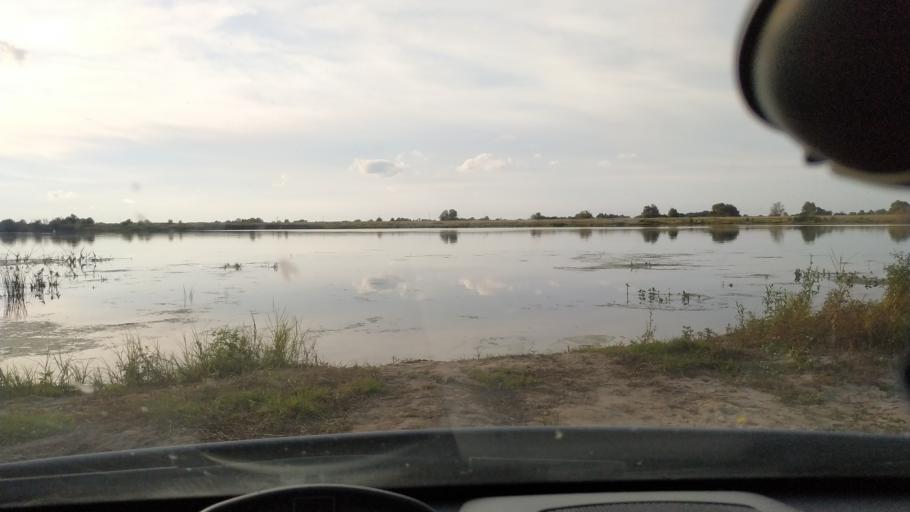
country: RU
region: Rjazan
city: Solotcha
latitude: 54.8718
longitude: 39.6532
